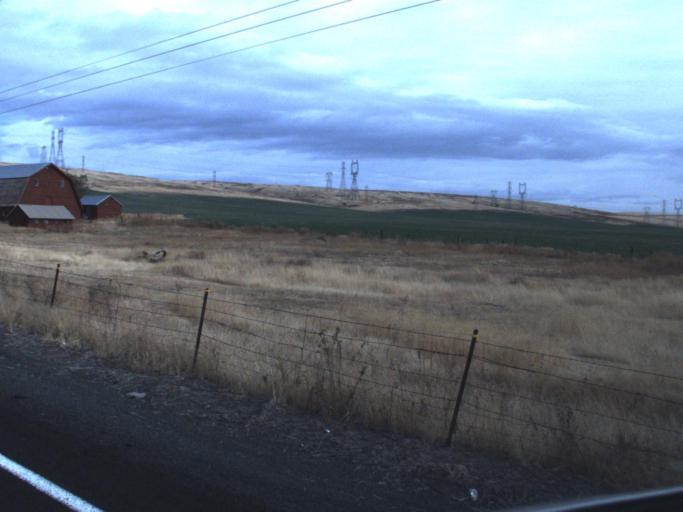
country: US
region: Washington
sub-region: Okanogan County
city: Coulee Dam
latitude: 47.8361
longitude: -118.7185
